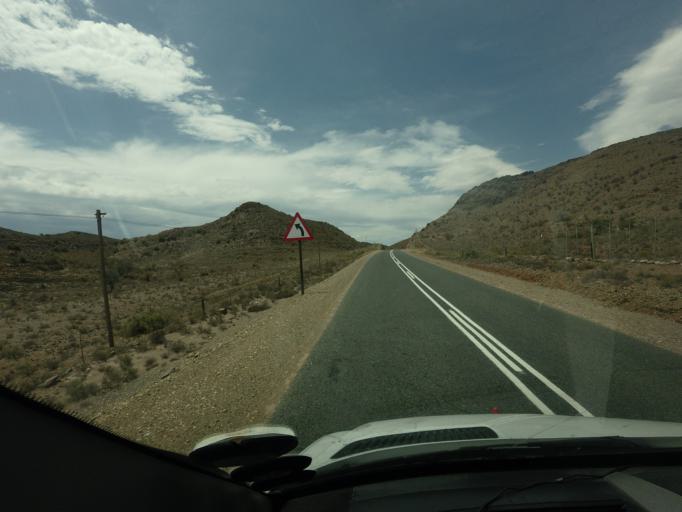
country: ZA
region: Western Cape
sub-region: Eden District Municipality
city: Ladismith
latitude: -33.7139
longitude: 20.9663
